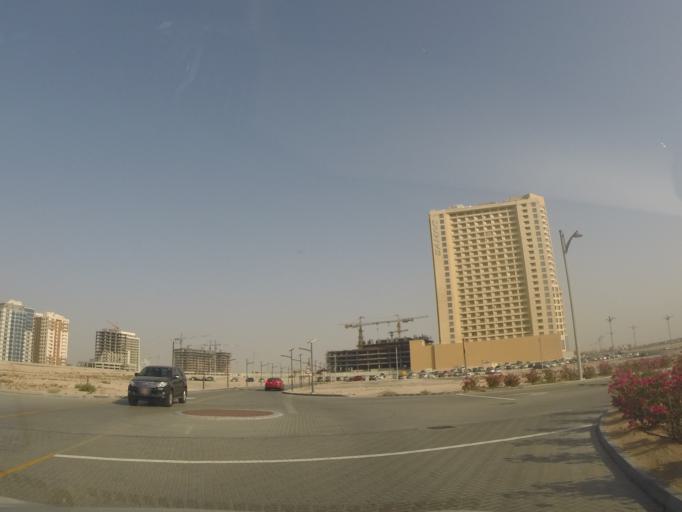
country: AE
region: Dubai
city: Dubai
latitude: 25.0389
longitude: 55.1998
